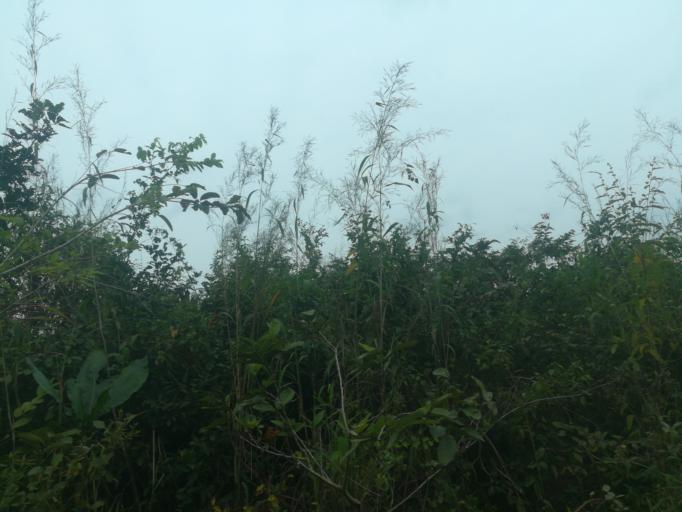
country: NG
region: Ogun
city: Itori
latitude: 7.1029
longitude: 3.1497
